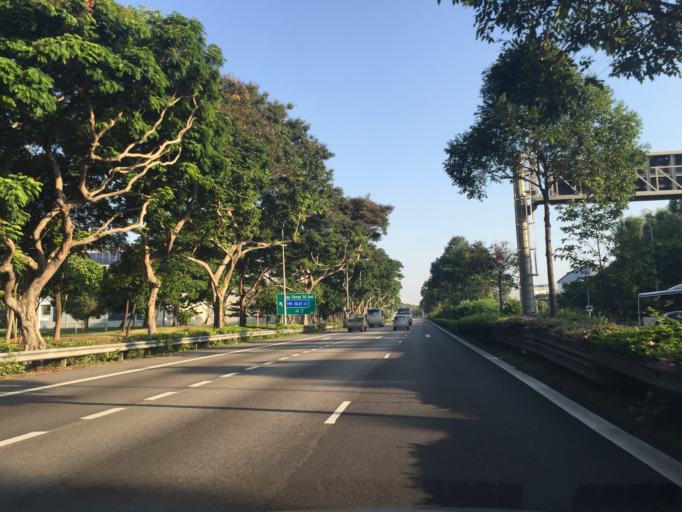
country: SG
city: Singapore
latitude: 1.3430
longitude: 103.9694
